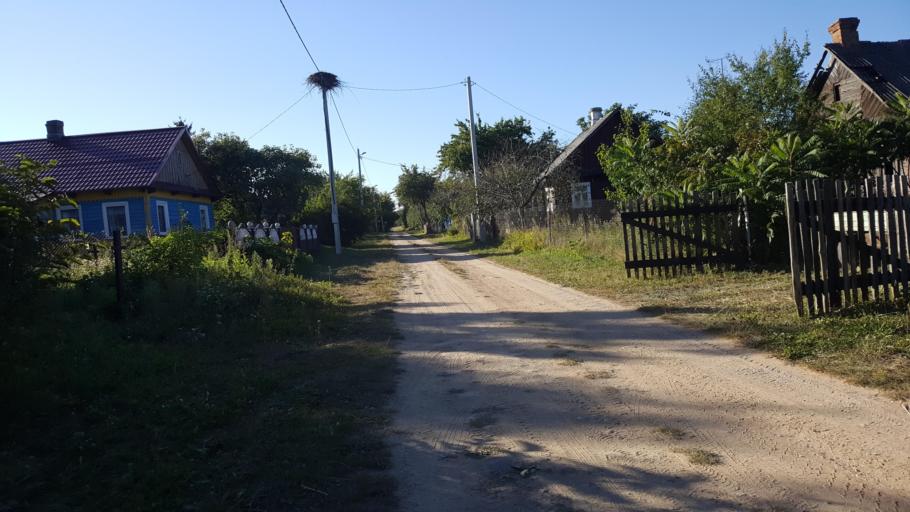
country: BY
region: Brest
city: Vysokaye
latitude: 52.3286
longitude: 23.2642
